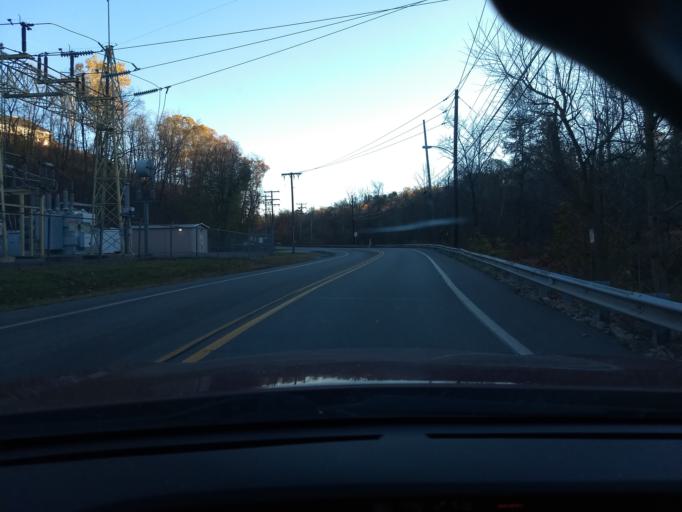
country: US
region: Pennsylvania
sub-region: Allegheny County
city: Upper Saint Clair
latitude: 40.3533
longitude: -80.0876
